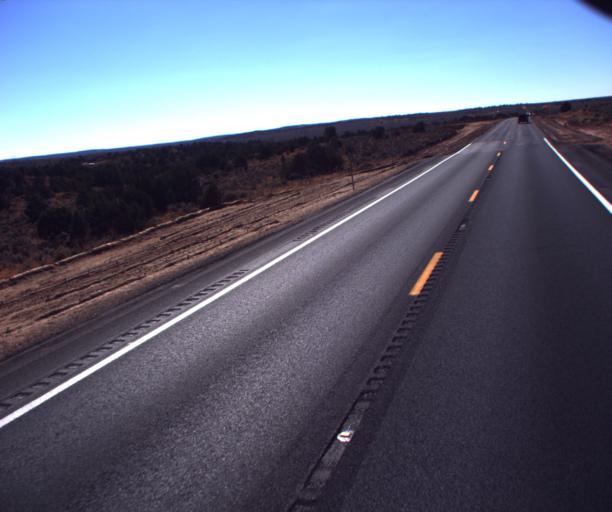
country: US
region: Arizona
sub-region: Apache County
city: Ganado
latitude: 35.7143
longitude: -109.4870
